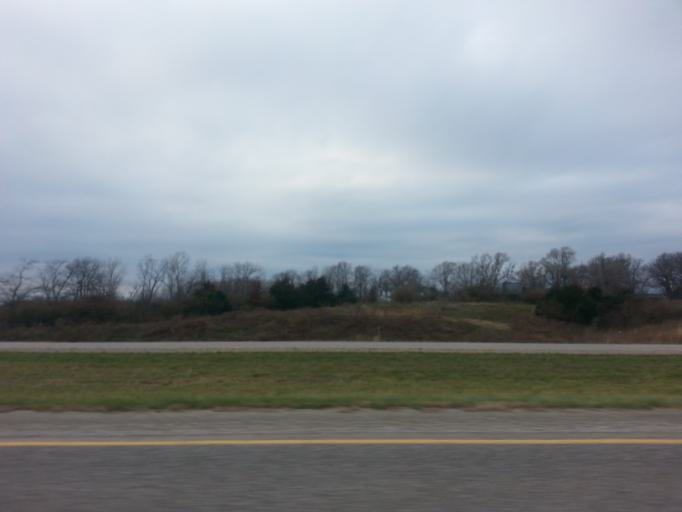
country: US
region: Iowa
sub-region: Henry County
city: Mount Pleasant
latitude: 40.9104
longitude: -91.5474
